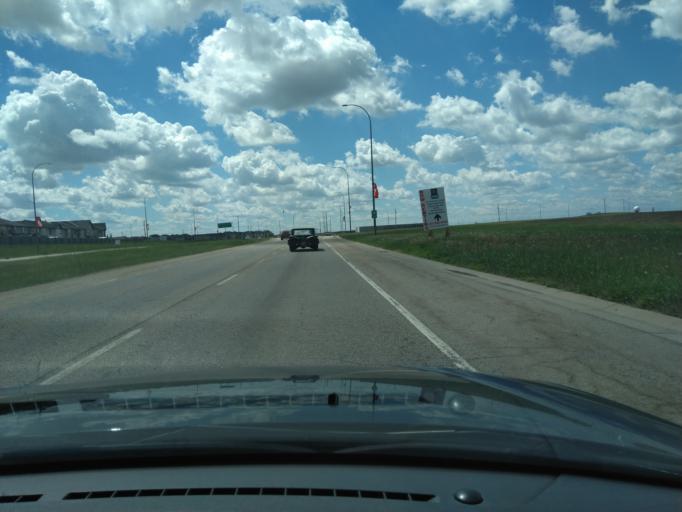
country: CA
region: Alberta
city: Airdrie
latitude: 51.1574
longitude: -113.9703
